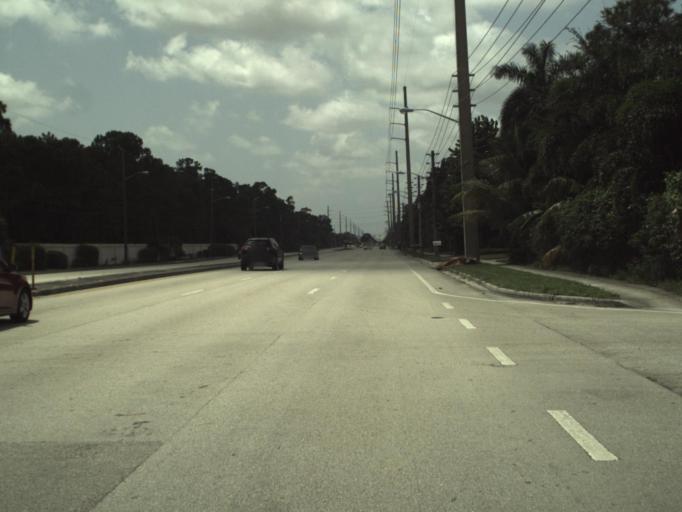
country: US
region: Florida
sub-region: Palm Beach County
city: Lake Belvedere Estates
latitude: 26.6689
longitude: -80.1453
